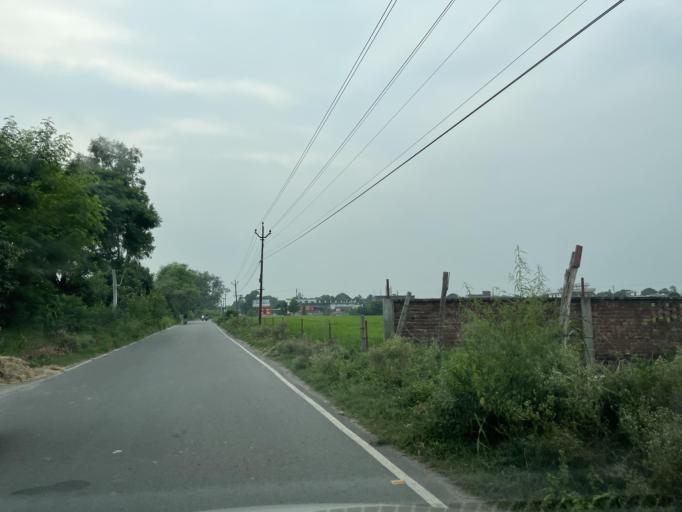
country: IN
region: Uttarakhand
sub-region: Naini Tal
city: Haldwani
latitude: 29.1730
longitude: 79.4831
